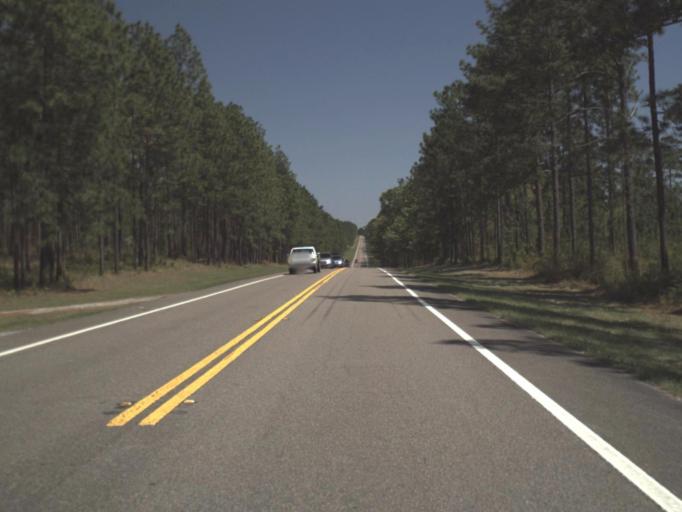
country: US
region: Florida
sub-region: Okaloosa County
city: Crestview
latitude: 30.8537
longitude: -86.8274
